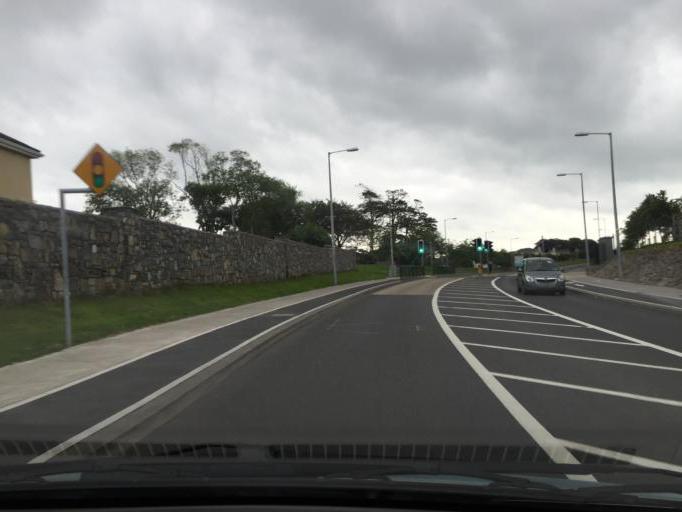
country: IE
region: Connaught
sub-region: Sligo
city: Sligo
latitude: 54.2699
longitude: -8.5028
